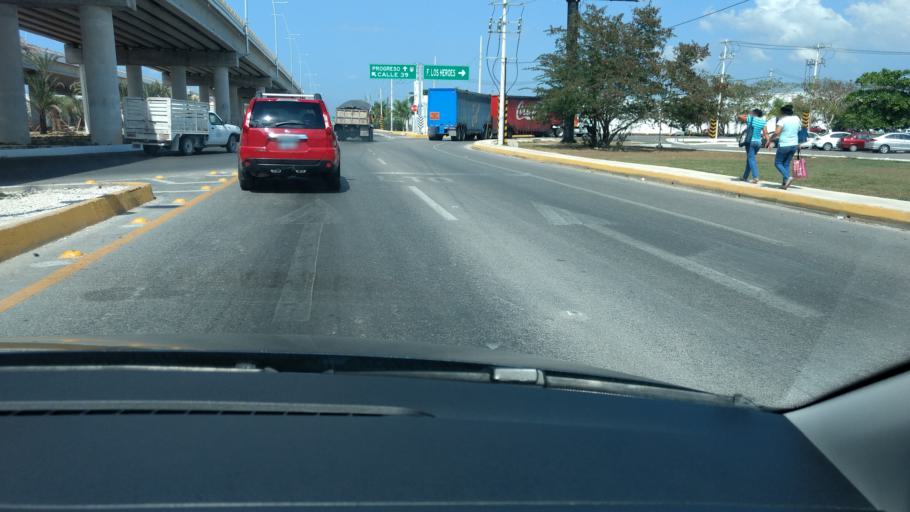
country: MX
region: Yucatan
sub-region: Kanasin
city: Kanasin
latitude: 20.9811
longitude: -89.5636
